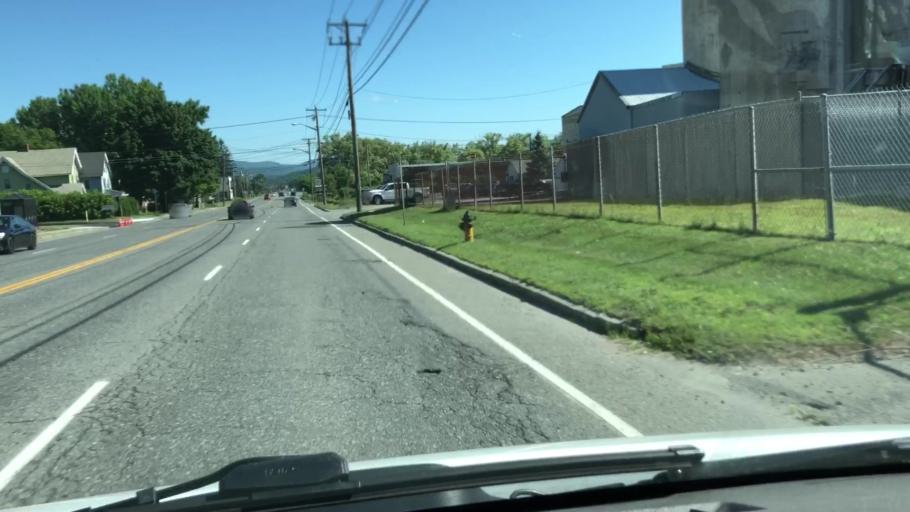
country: US
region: Massachusetts
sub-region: Berkshire County
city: Adams
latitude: 42.6534
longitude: -73.1103
